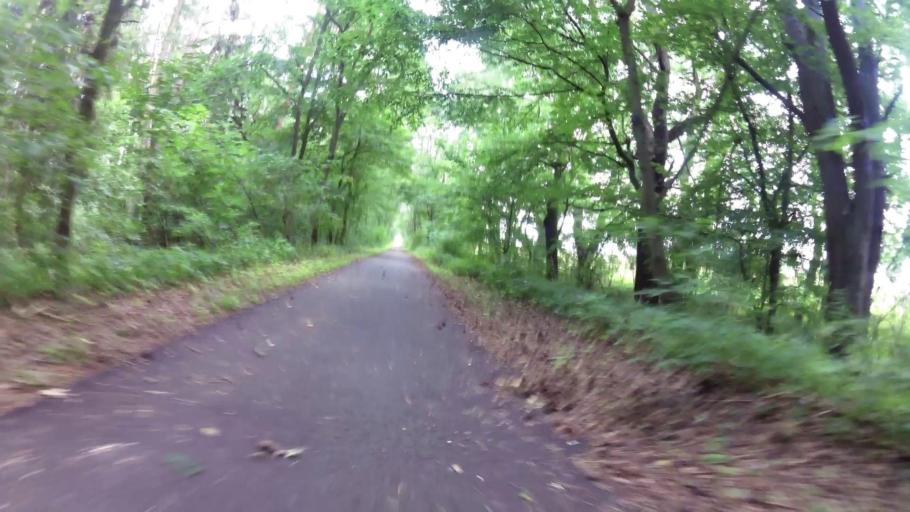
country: PL
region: West Pomeranian Voivodeship
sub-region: Powiat gryfinski
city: Banie
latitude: 53.0524
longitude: 14.6287
